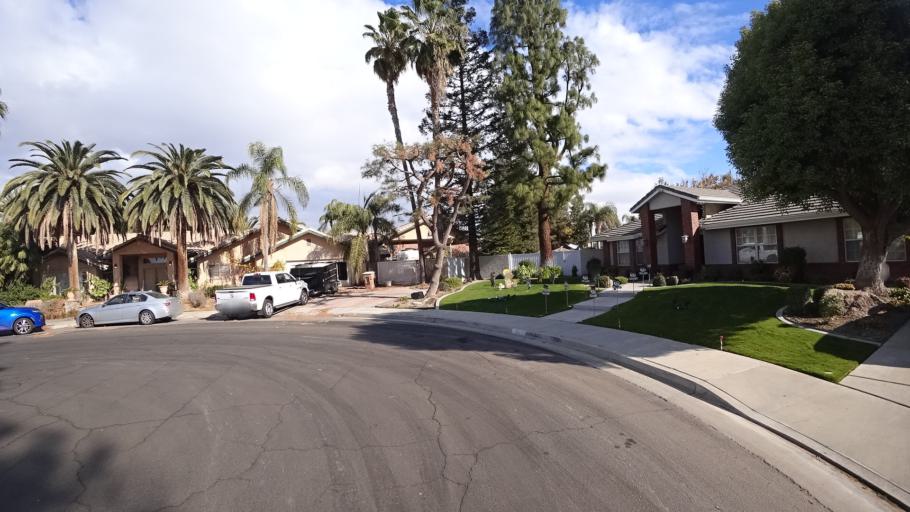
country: US
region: California
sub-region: Kern County
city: Greenacres
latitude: 35.3391
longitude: -119.0850
